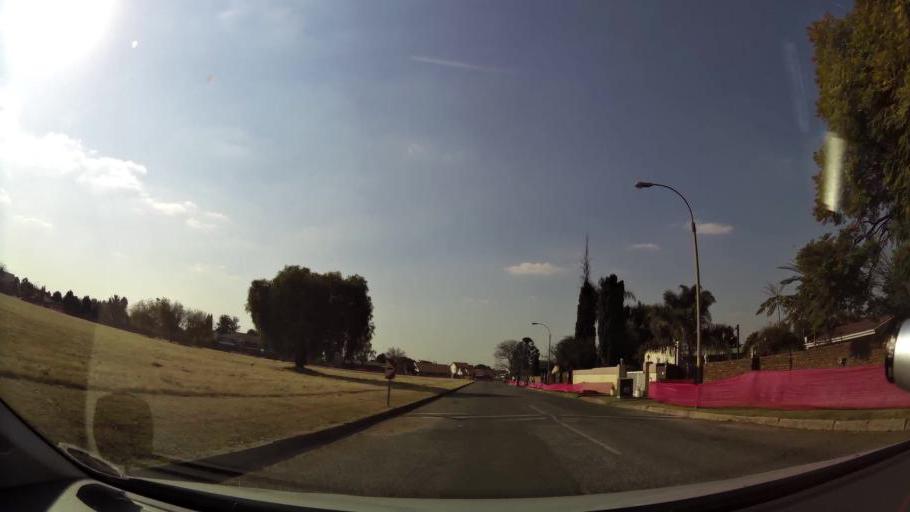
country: ZA
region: Gauteng
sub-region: City of Johannesburg Metropolitan Municipality
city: Modderfontein
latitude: -26.0928
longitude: 28.2035
